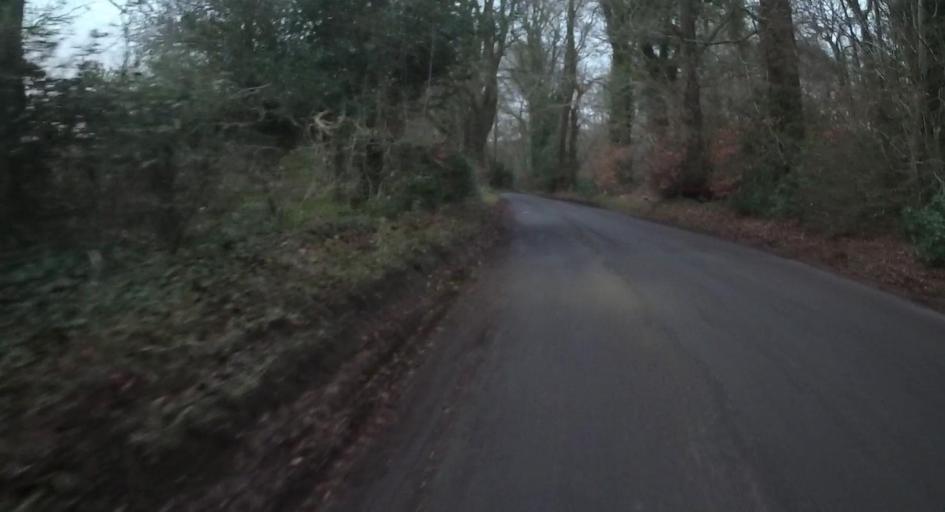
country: GB
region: England
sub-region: Hampshire
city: Four Marks
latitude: 51.0579
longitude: -1.0991
